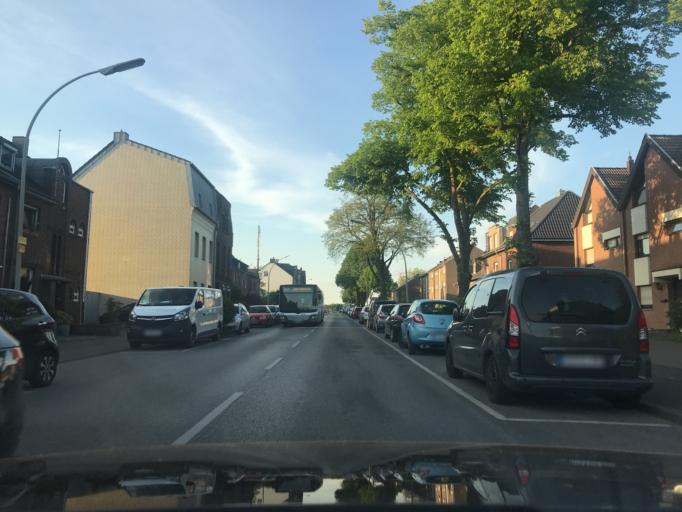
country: DE
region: North Rhine-Westphalia
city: Wegberg
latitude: 51.1535
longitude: 6.3653
